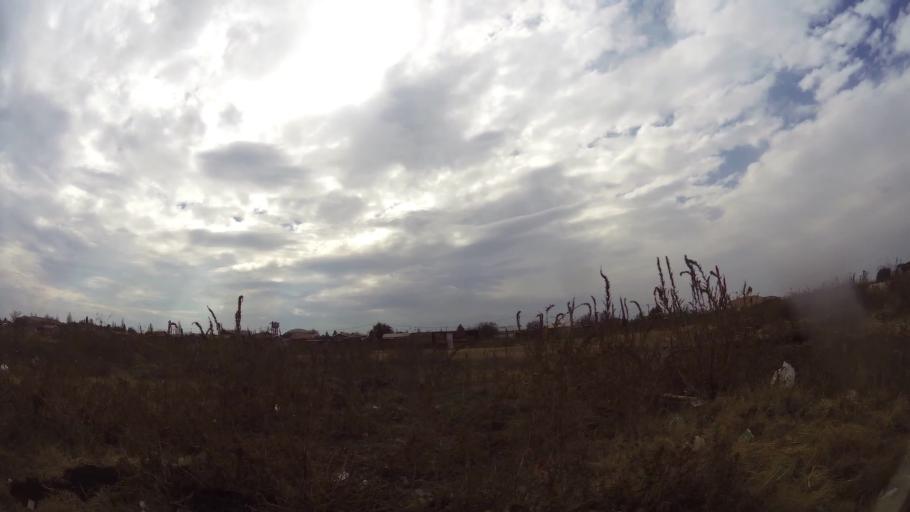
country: ZA
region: Gauteng
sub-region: Ekurhuleni Metropolitan Municipality
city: Germiston
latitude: -26.3974
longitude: 28.1529
